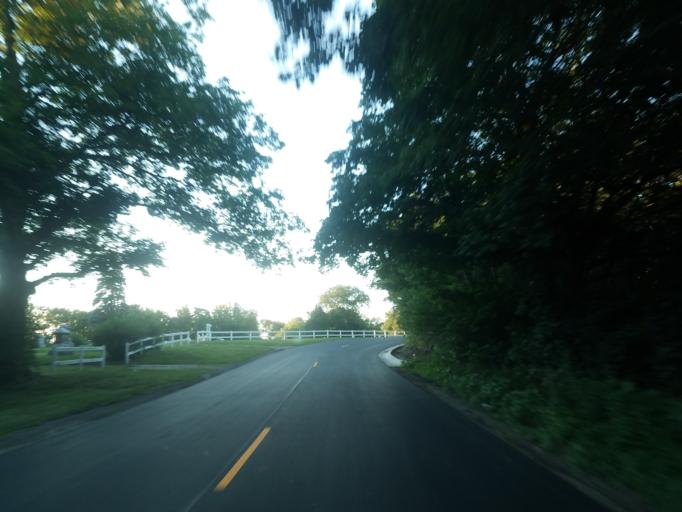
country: US
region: Illinois
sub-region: McLean County
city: Bloomington
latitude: 40.4538
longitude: -89.0382
